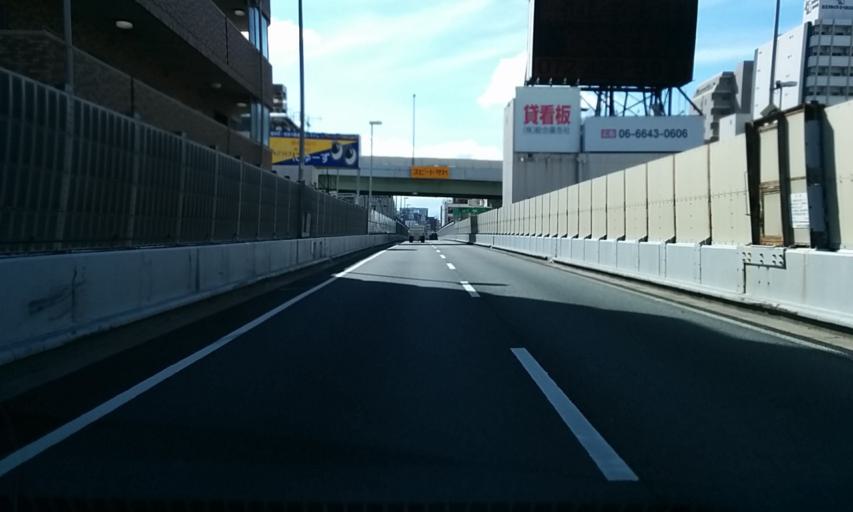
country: JP
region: Osaka
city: Osaka-shi
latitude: 34.6676
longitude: 135.5104
